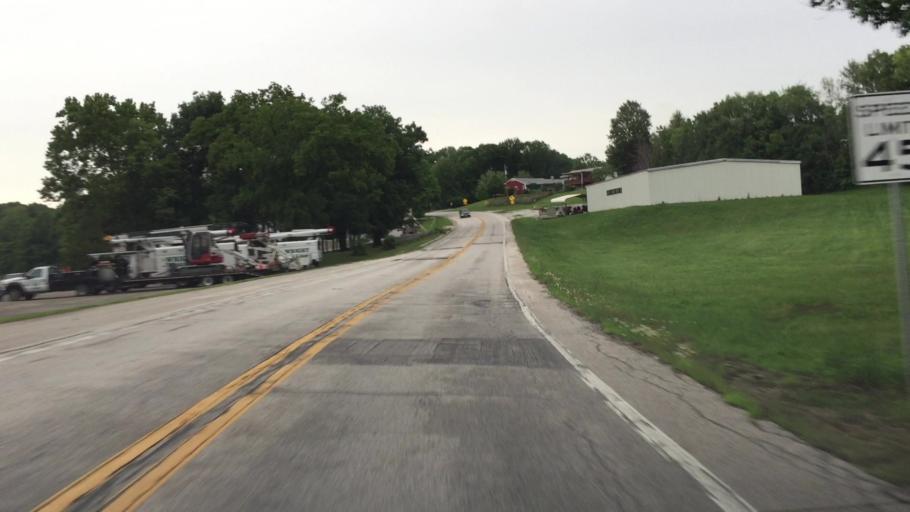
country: US
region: Illinois
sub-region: Hancock County
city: Hamilton
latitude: 40.4051
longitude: -91.3517
